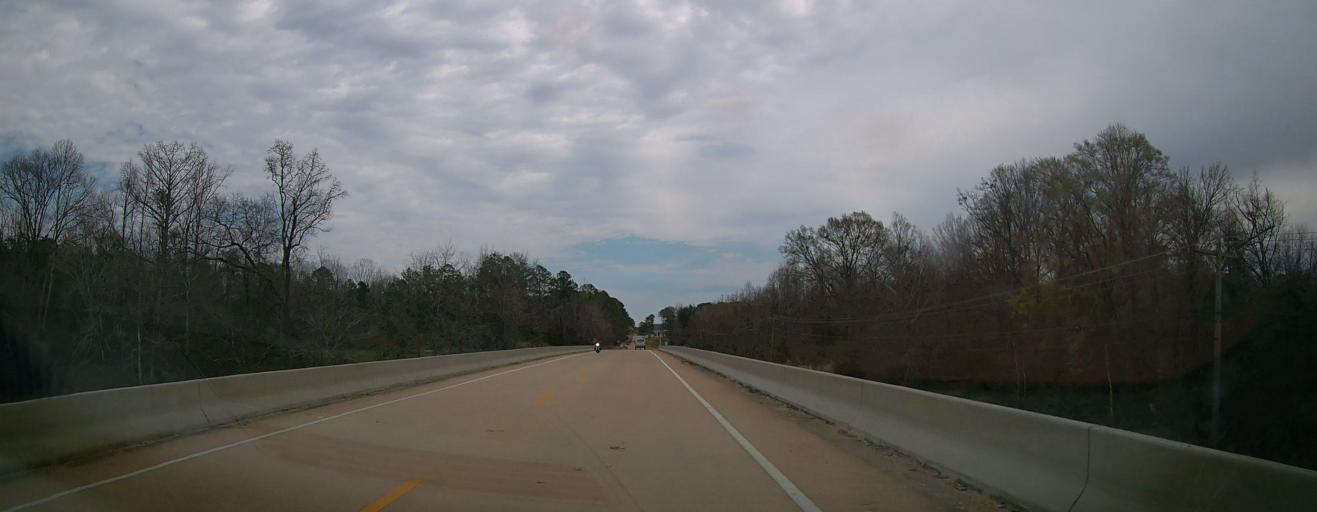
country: US
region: Mississippi
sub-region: Itawamba County
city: Fulton
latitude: 34.2394
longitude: -88.2722
